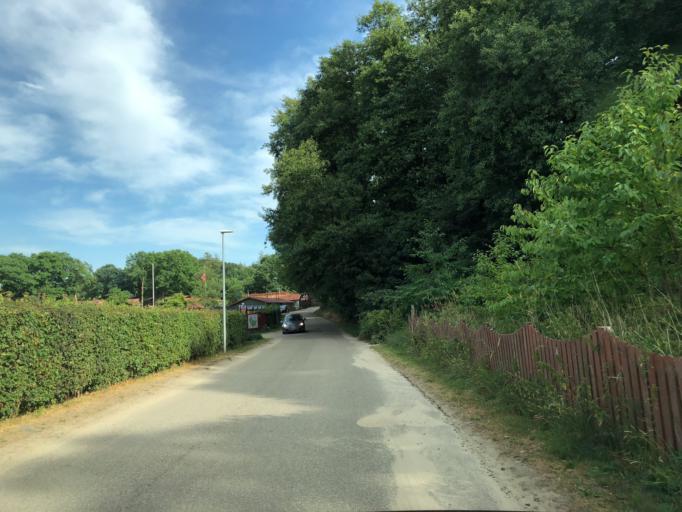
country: DK
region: South Denmark
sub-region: Vejle Kommune
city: Egtved
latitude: 55.6897
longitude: 9.2666
